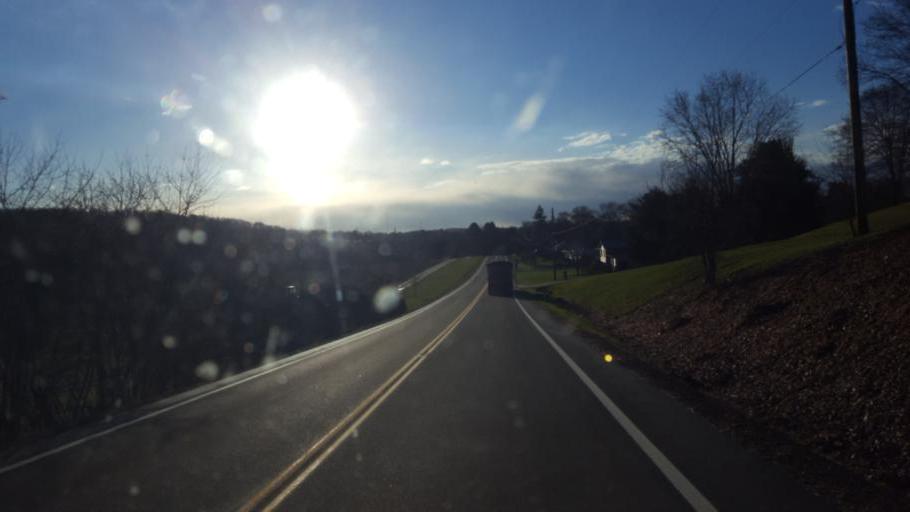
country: US
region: Ohio
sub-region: Ashland County
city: Loudonville
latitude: 40.6493
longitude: -82.2517
